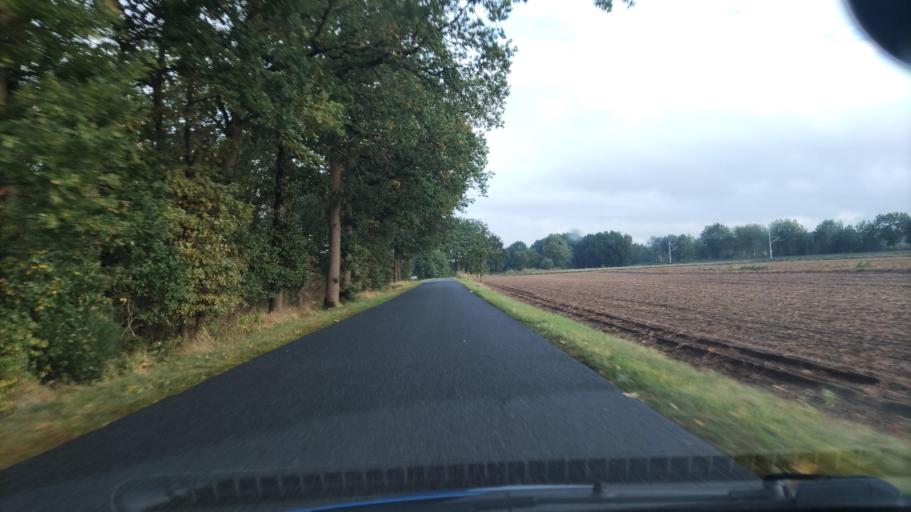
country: DE
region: Lower Saxony
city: Wrestedt
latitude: 52.9043
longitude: 10.6080
